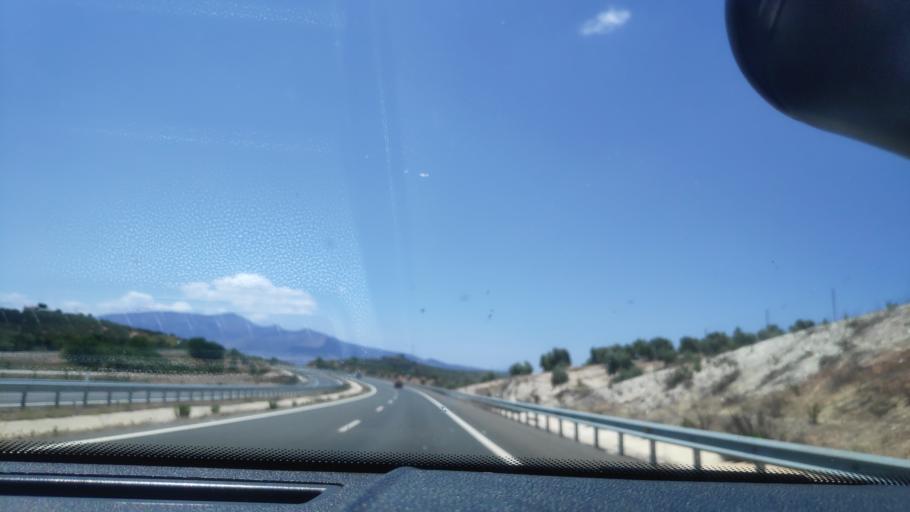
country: ES
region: Andalusia
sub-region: Provincia de Jaen
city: La Guardia de Jaen
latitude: 37.8064
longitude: -3.6770
